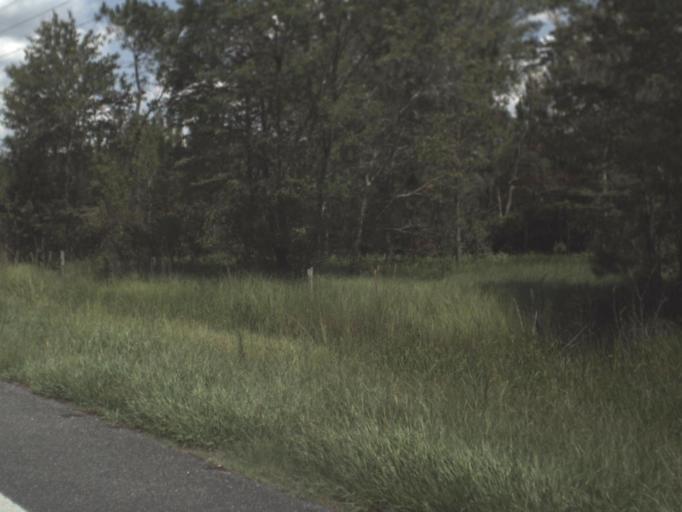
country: US
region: Florida
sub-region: Gilchrist County
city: Trenton
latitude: 29.6192
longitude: -82.7733
